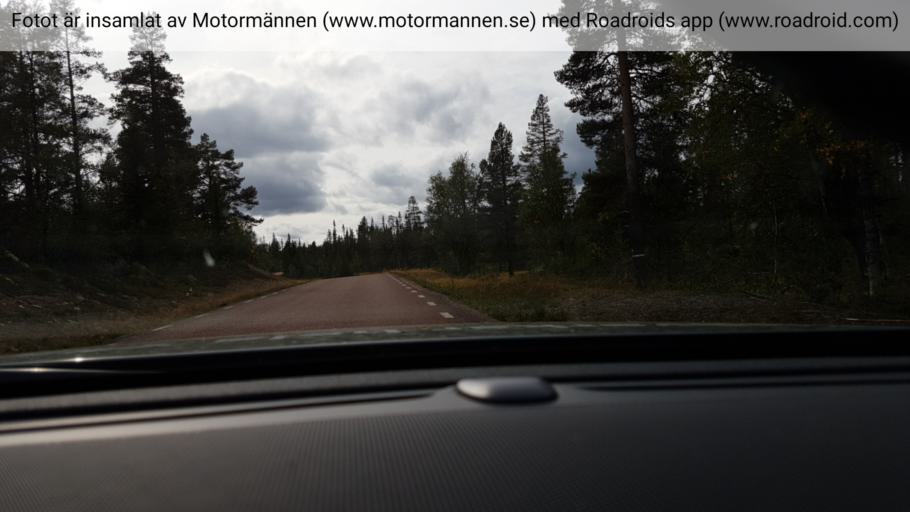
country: NO
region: Hedmark
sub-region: Trysil
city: Innbygda
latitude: 61.6855
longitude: 12.5281
